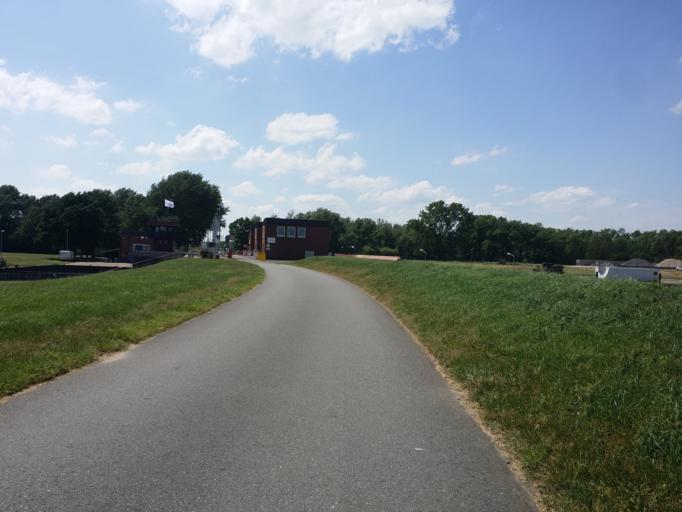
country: DE
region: Lower Saxony
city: Lemwerder
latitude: 53.1235
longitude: 8.6508
